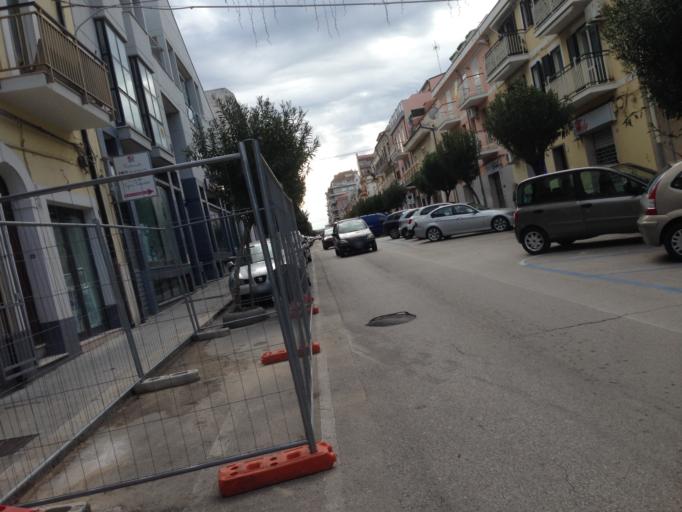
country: IT
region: Molise
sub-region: Provincia di Campobasso
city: Termoli
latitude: 42.0023
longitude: 14.9968
